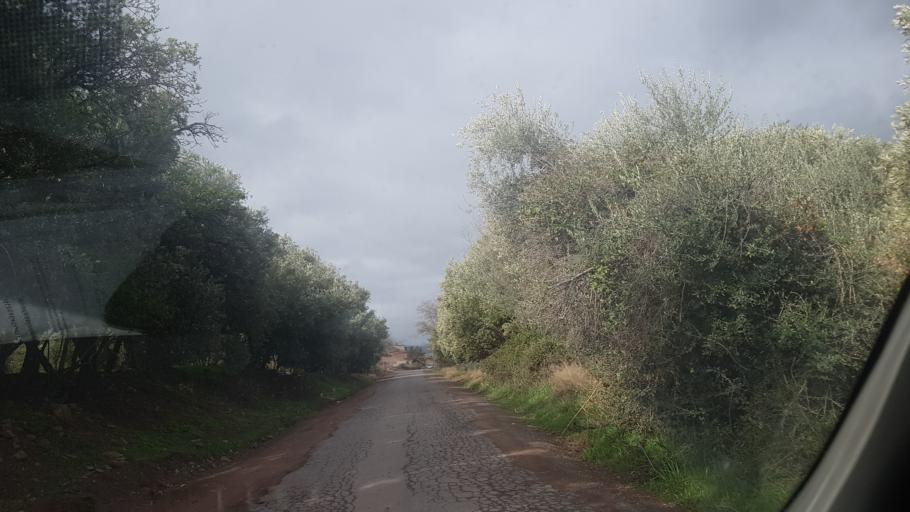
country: MA
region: Marrakech-Tensift-Al Haouz
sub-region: Al-Haouz
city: Azgour
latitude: 30.9993
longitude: -8.1621
